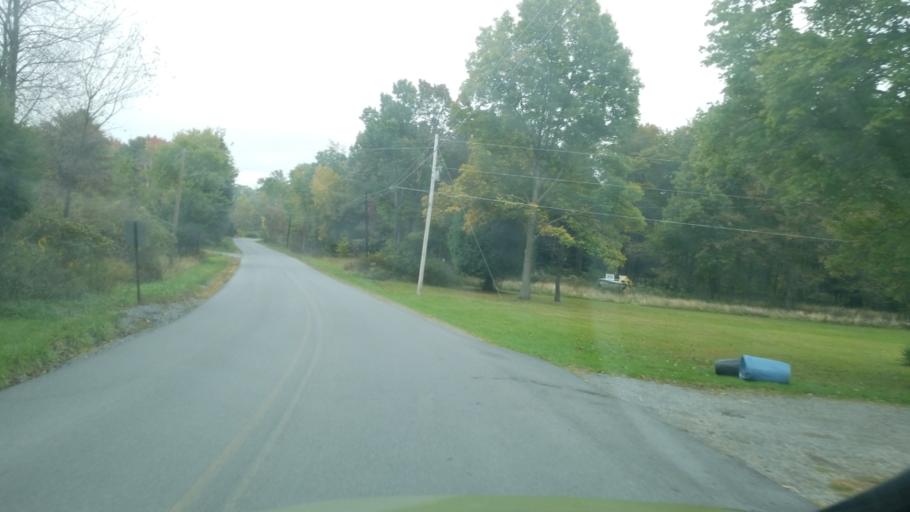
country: US
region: Pennsylvania
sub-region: Clearfield County
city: Curwensville
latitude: 41.0232
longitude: -78.5552
